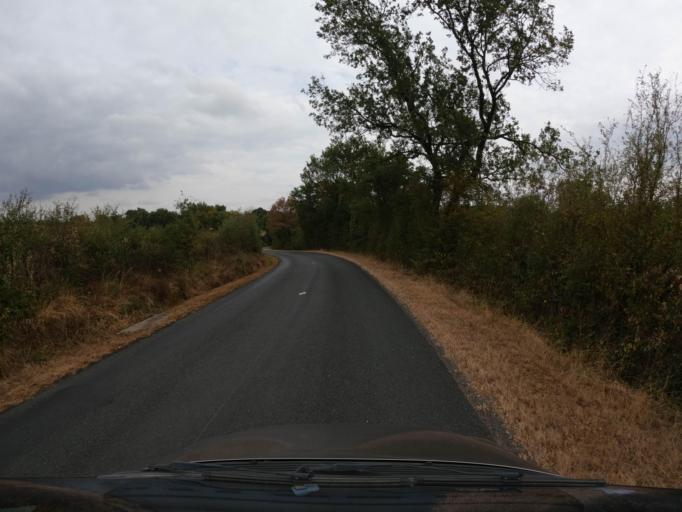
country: FR
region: Pays de la Loire
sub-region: Departement de la Vendee
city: Tiffauges
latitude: 46.9938
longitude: -1.1100
